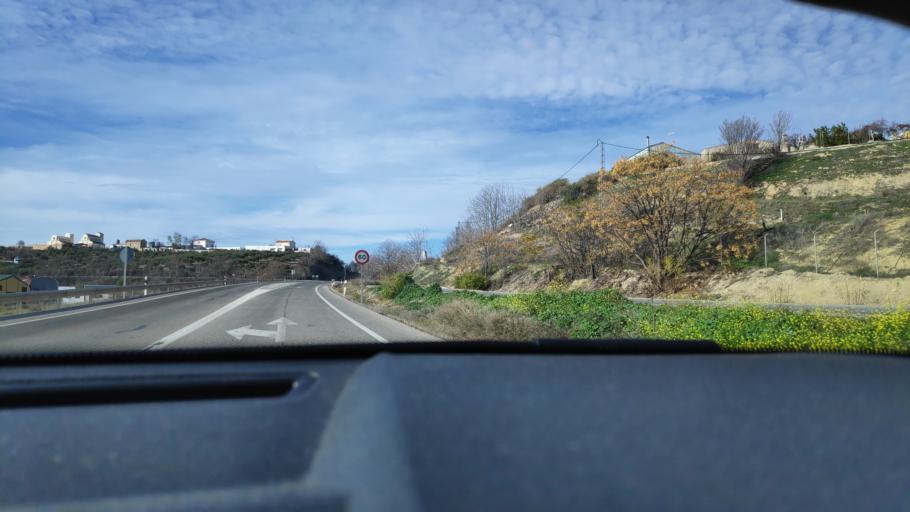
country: ES
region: Andalusia
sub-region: Provincia de Jaen
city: Porcuna
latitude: 37.8702
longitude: -4.1677
